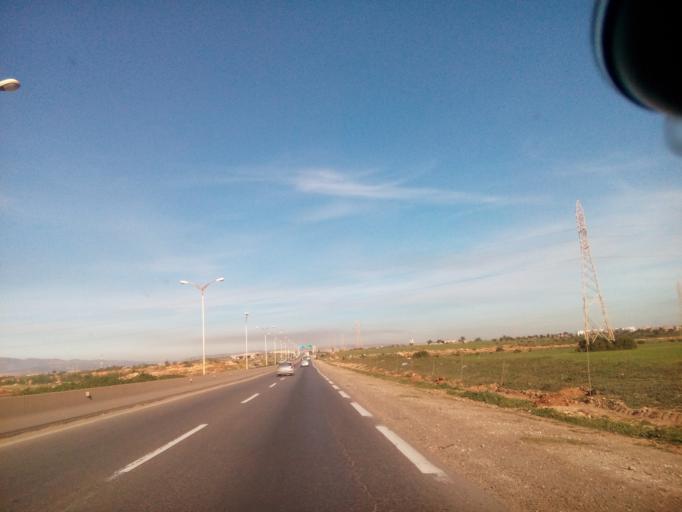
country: DZ
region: Oran
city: Ain el Bya
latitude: 35.7920
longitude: -0.2885
